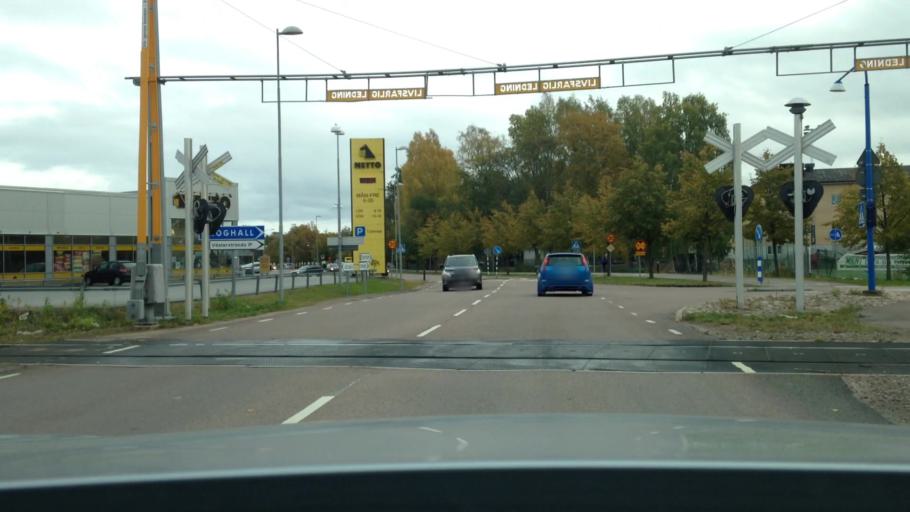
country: SE
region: Vaermland
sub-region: Karlstads Kommun
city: Karlstad
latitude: 59.3808
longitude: 13.4694
